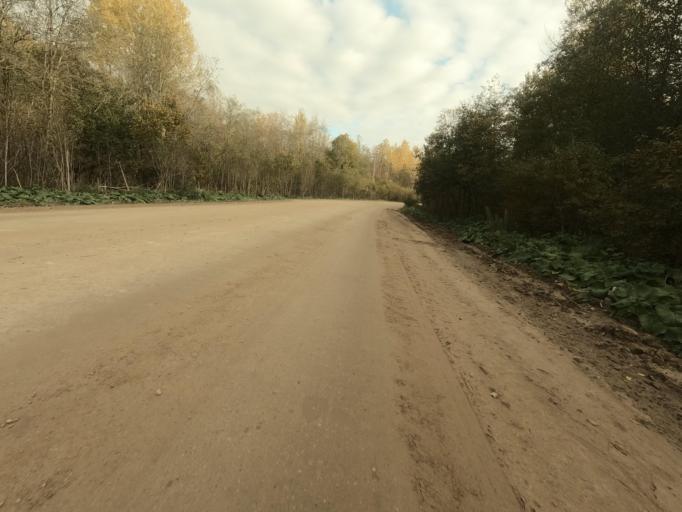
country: RU
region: Novgorod
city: Batetskiy
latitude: 58.8021
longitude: 30.6440
